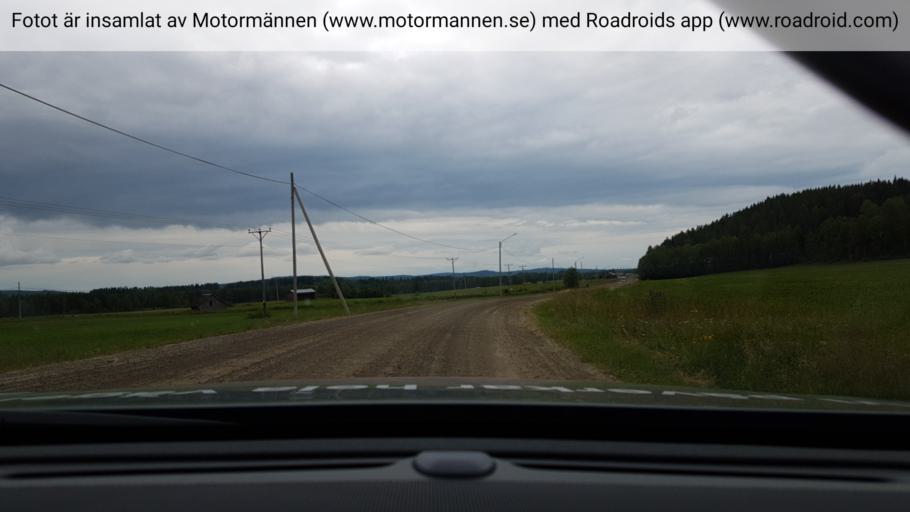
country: SE
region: Vaesterbotten
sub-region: Vannas Kommun
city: Vannasby
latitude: 64.1011
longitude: 19.9896
